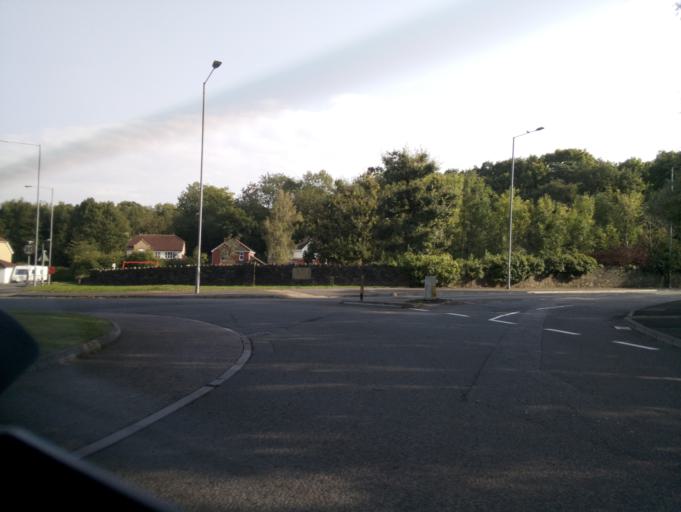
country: GB
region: Wales
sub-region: Torfaen County Borough
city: Cwmbran
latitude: 51.6305
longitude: -3.0062
